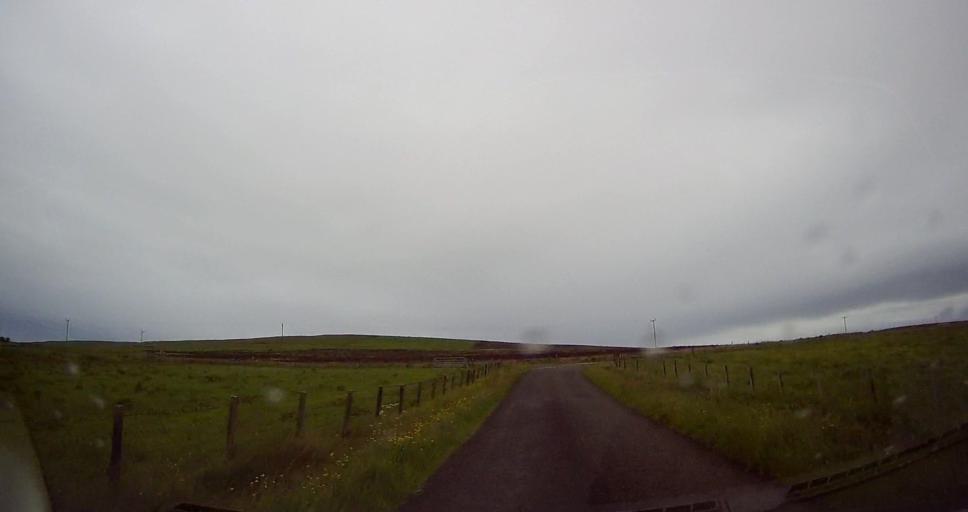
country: GB
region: Scotland
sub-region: Orkney Islands
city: Stromness
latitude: 59.0920
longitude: -3.1827
